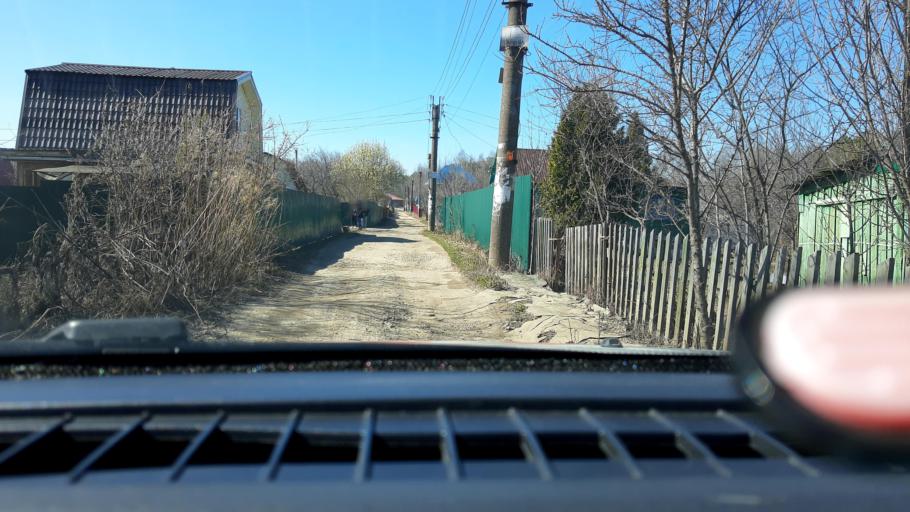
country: RU
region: Nizjnij Novgorod
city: Neklyudovo
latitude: 56.4327
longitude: 43.9976
